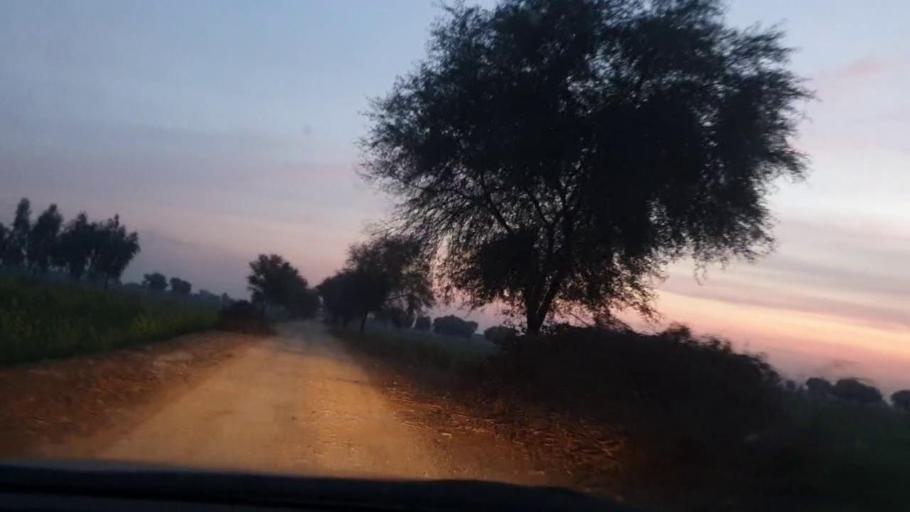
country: PK
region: Sindh
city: Sakrand
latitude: 26.1931
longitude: 68.3015
